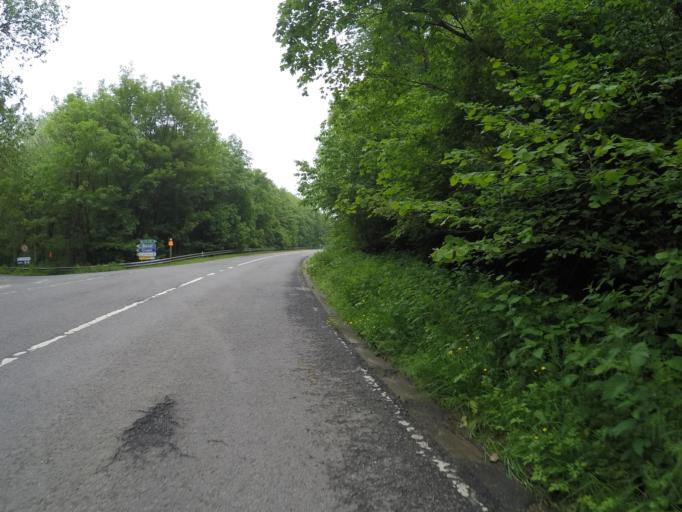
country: BE
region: Wallonia
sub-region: Province de Namur
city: Assesse
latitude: 50.3321
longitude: 5.0055
